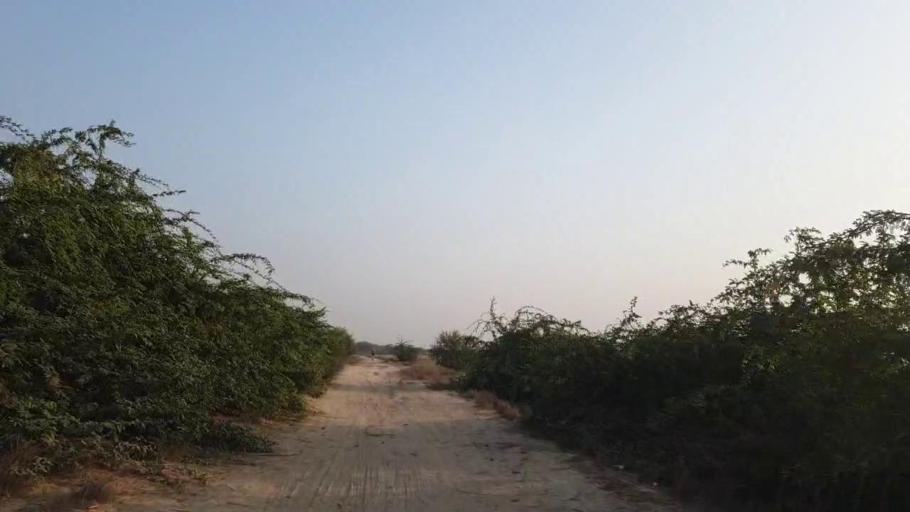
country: PK
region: Sindh
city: Kario
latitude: 24.8546
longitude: 68.6283
